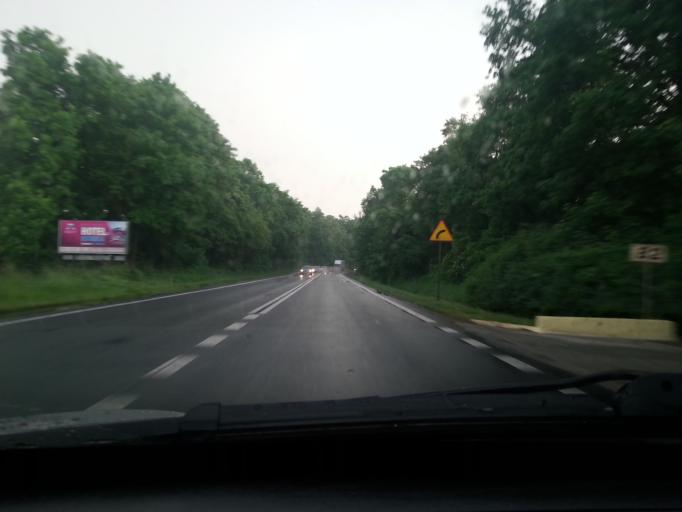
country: PL
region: Lodz Voivodeship
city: Lodz
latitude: 51.8099
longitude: 19.5020
